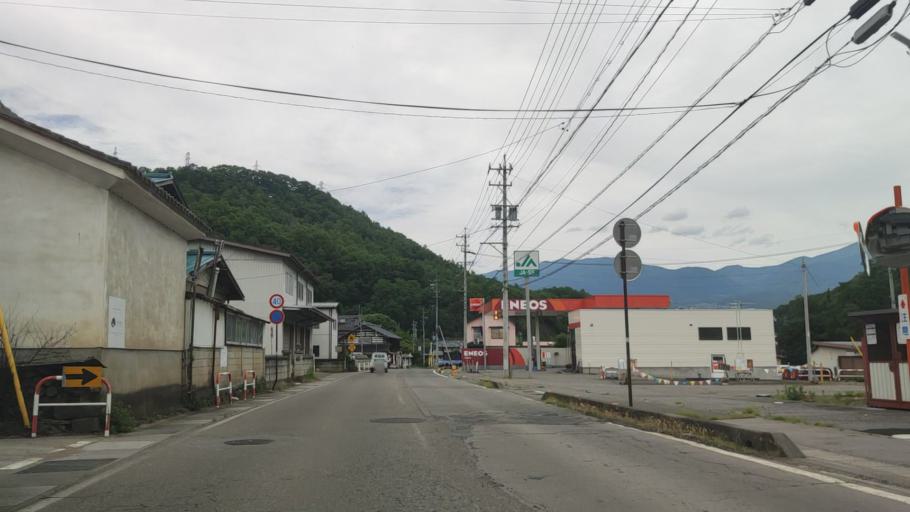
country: JP
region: Nagano
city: Kamimaruko
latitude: 36.3298
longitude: 138.3465
